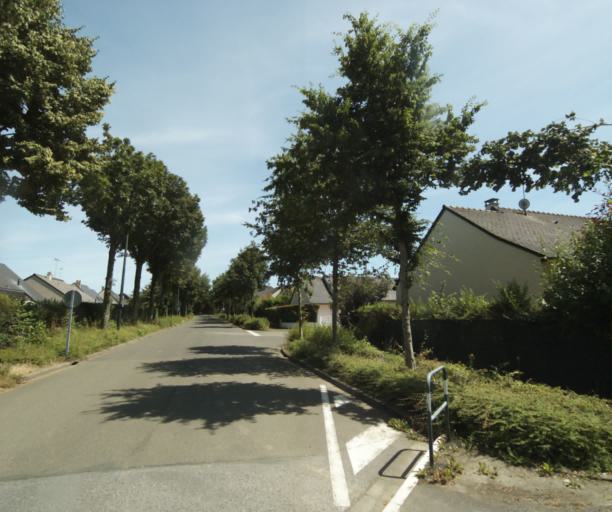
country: FR
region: Pays de la Loire
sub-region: Departement de la Mayenne
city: Change
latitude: 48.0801
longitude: -0.8070
